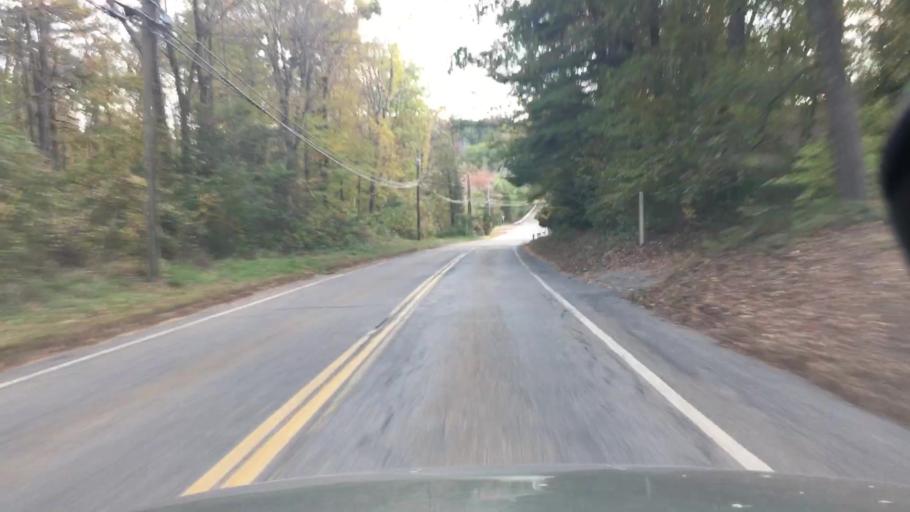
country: US
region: Connecticut
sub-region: Tolland County
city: Stafford
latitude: 41.9427
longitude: -72.1919
